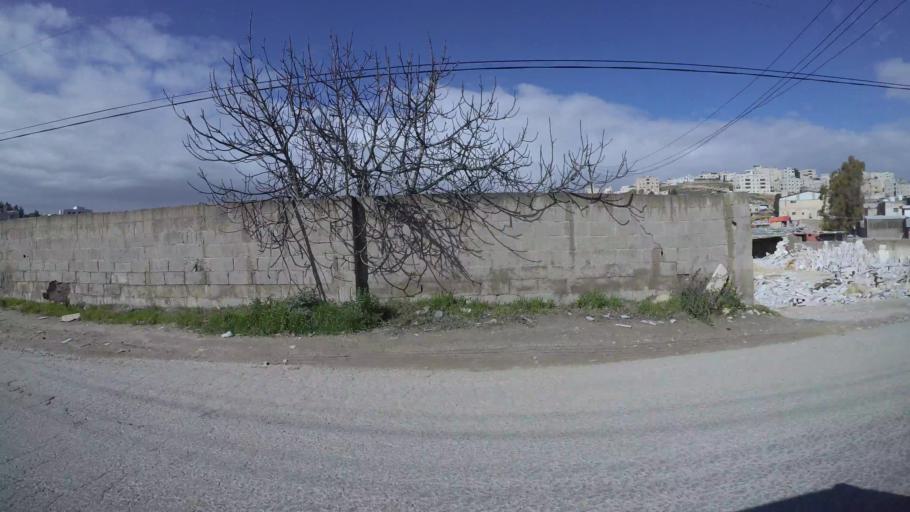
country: JO
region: Amman
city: Al Jubayhah
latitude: 32.0135
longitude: 35.8447
